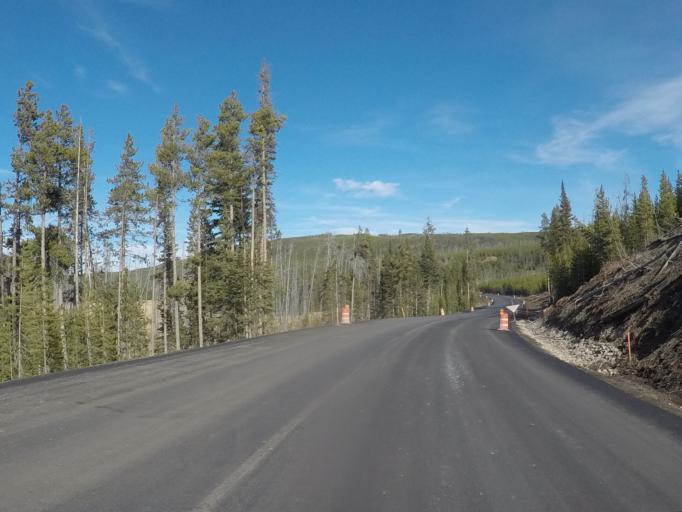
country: US
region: Montana
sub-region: Gallatin County
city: West Yellowstone
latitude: 44.8027
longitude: -110.7435
